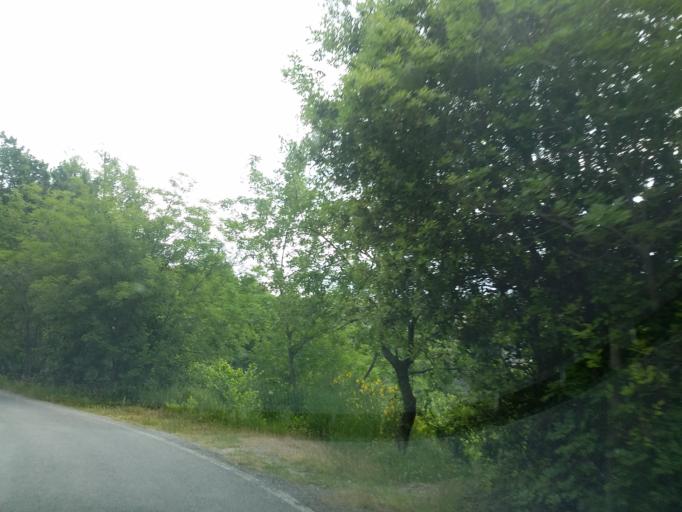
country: IT
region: Liguria
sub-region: Provincia di Savona
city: Orco Feglino
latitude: 44.2224
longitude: 8.3421
